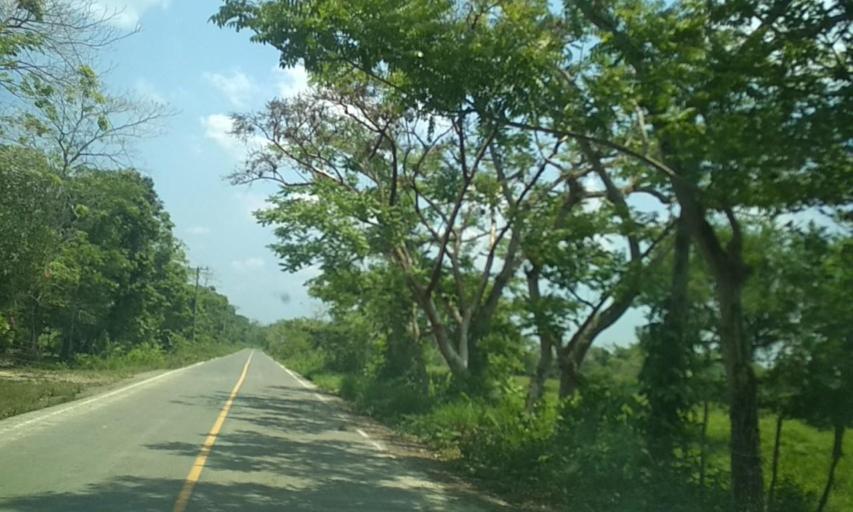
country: MX
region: Tabasco
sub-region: Huimanguillo
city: Francisco Rueda
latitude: 17.7591
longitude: -94.0240
